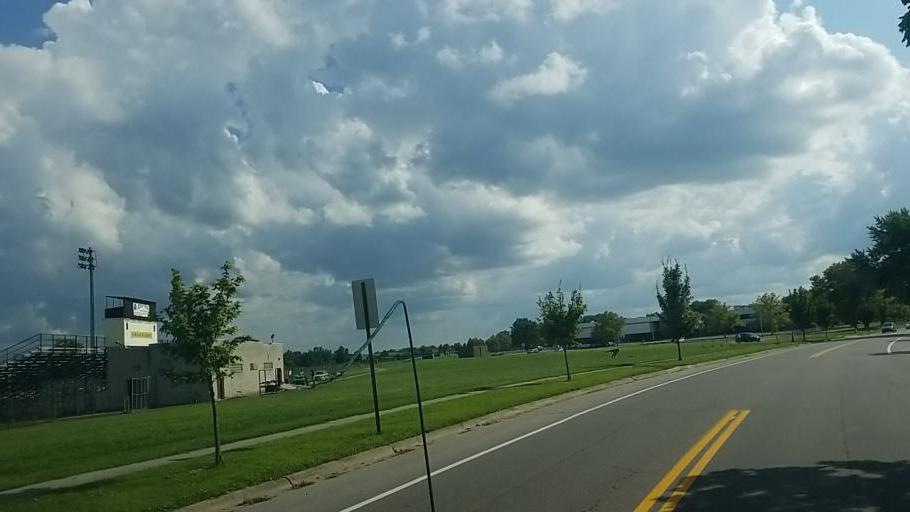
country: US
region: Ohio
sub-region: Franklin County
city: Minerva Park
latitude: 40.0970
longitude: -82.9633
